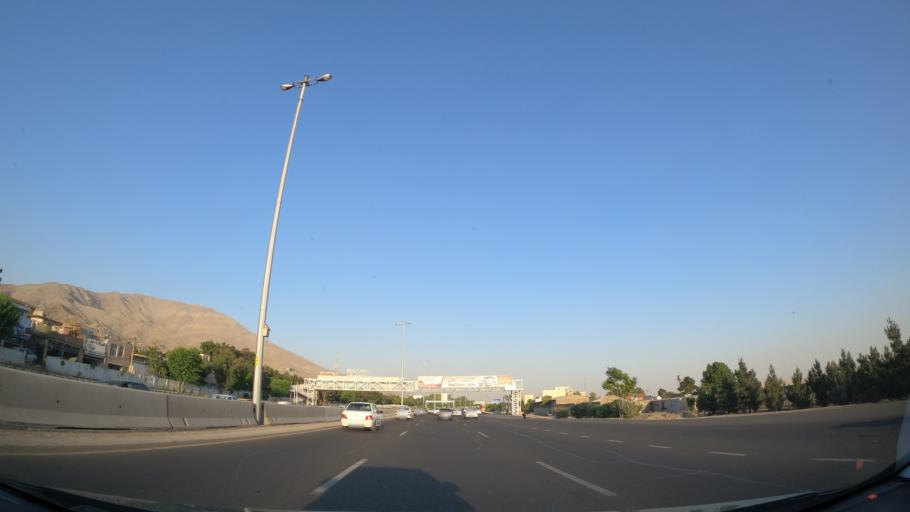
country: IR
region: Alborz
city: Karaj
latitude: 35.7870
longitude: 51.0235
